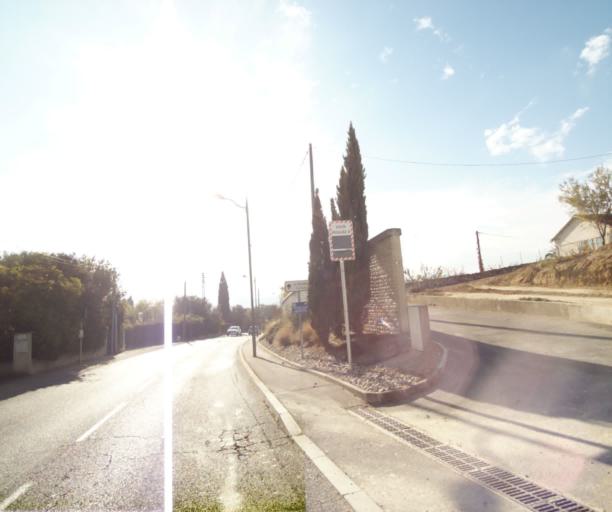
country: FR
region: Provence-Alpes-Cote d'Azur
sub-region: Departement des Bouches-du-Rhone
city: Allauch
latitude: 43.3250
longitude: 5.4918
